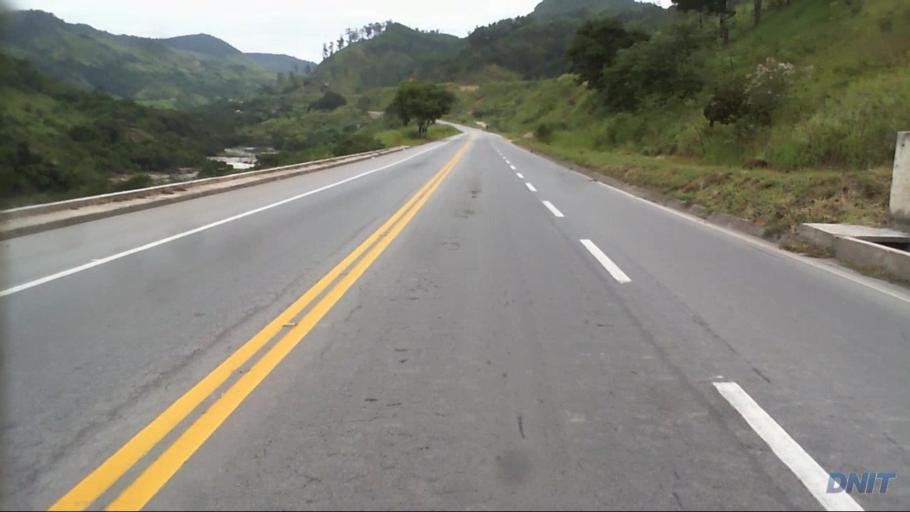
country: BR
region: Minas Gerais
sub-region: Timoteo
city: Timoteo
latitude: -19.6217
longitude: -42.8034
